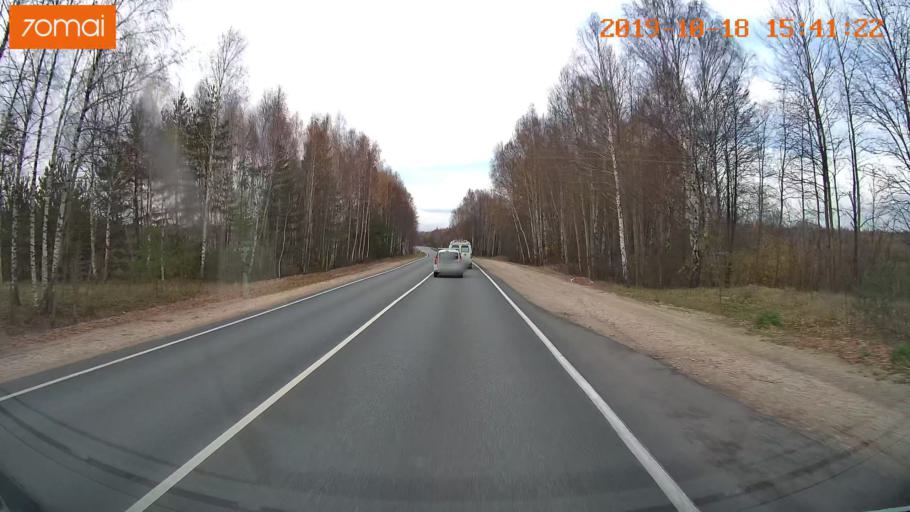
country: RU
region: Vladimir
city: Golovino
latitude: 55.9448
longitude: 40.5838
